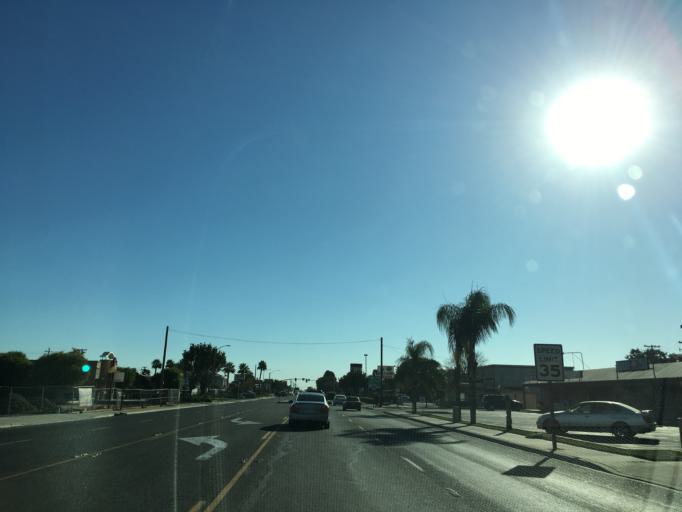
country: US
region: California
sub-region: Merced County
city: Los Banos
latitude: 37.0569
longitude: -120.8384
